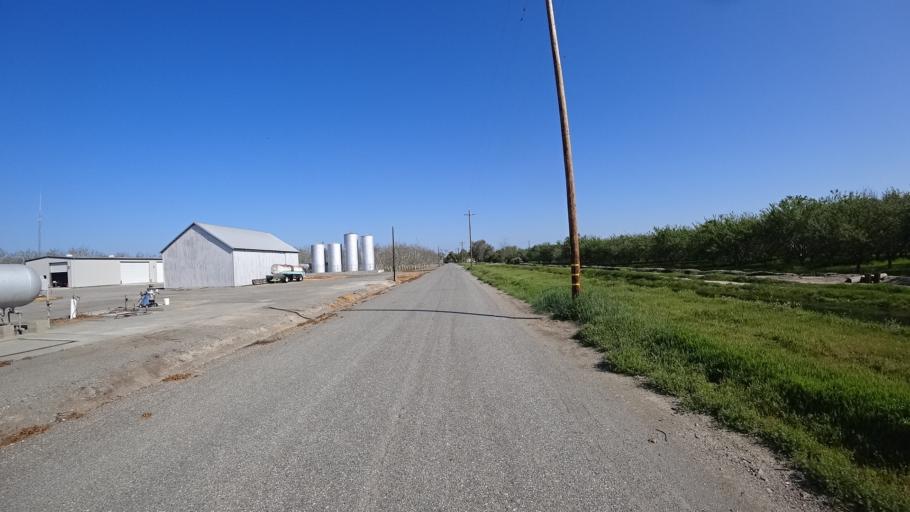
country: US
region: California
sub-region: Glenn County
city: Hamilton City
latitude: 39.6352
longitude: -122.0274
